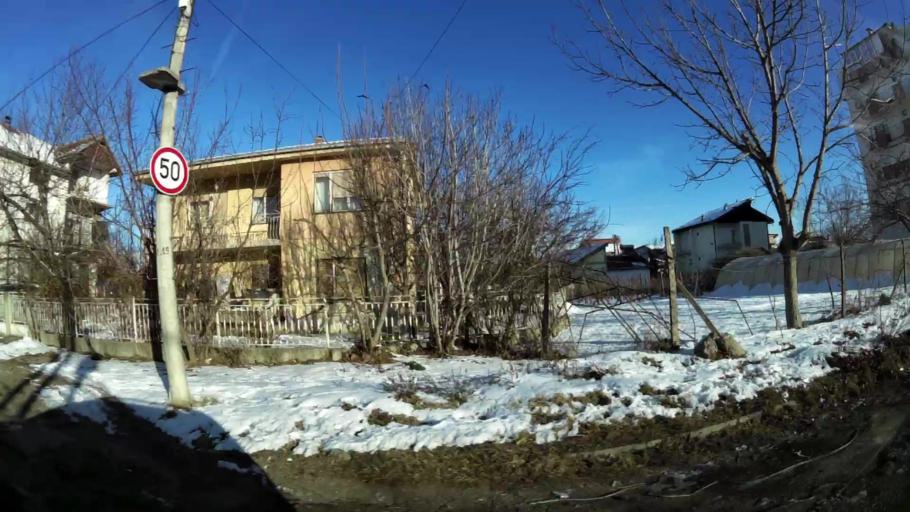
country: MK
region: Saraj
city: Saraj
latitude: 42.0086
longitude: 21.3459
